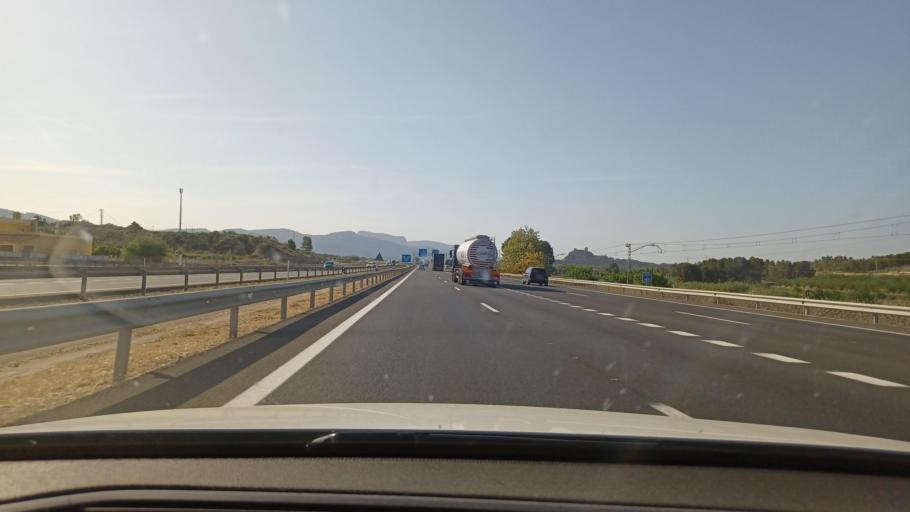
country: ES
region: Valencia
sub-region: Provincia de Alicante
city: Sax
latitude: 38.5595
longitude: -0.8290
